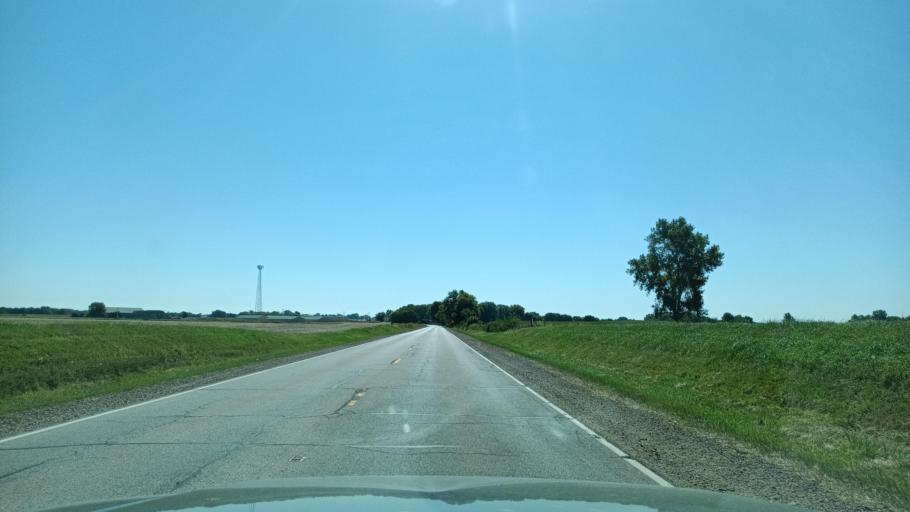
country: US
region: Illinois
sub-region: Peoria County
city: Elmwood
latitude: 40.8361
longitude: -89.8768
